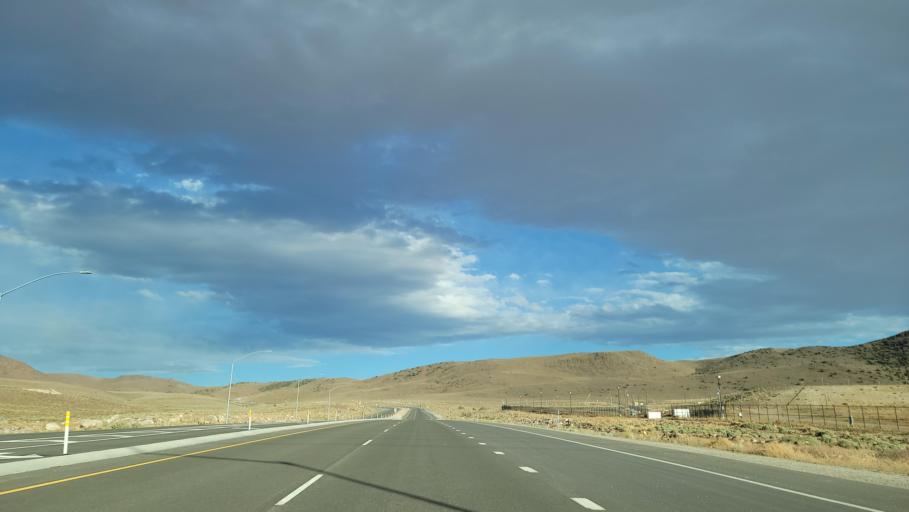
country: US
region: Nevada
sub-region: Lyon County
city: Stagecoach
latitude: 39.5012
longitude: -119.4288
